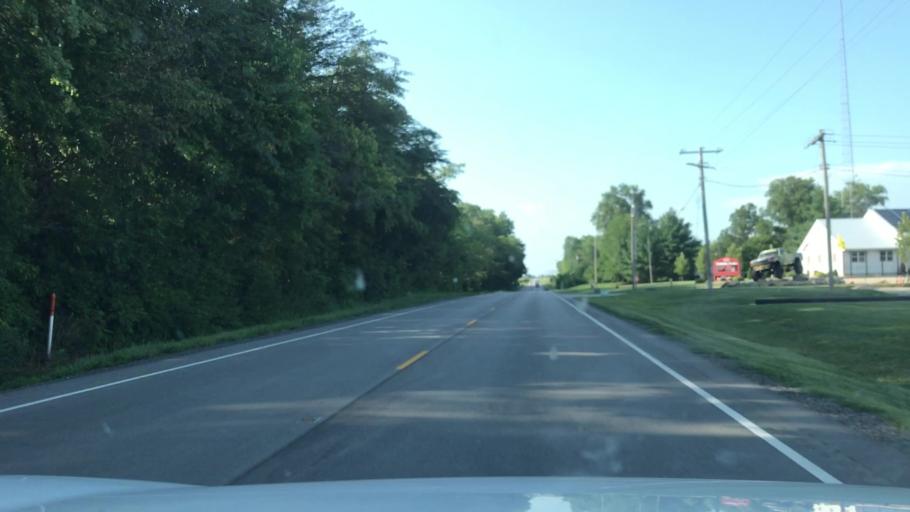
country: US
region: Illinois
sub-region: Washington County
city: Nashville
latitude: 38.3993
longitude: -89.3709
